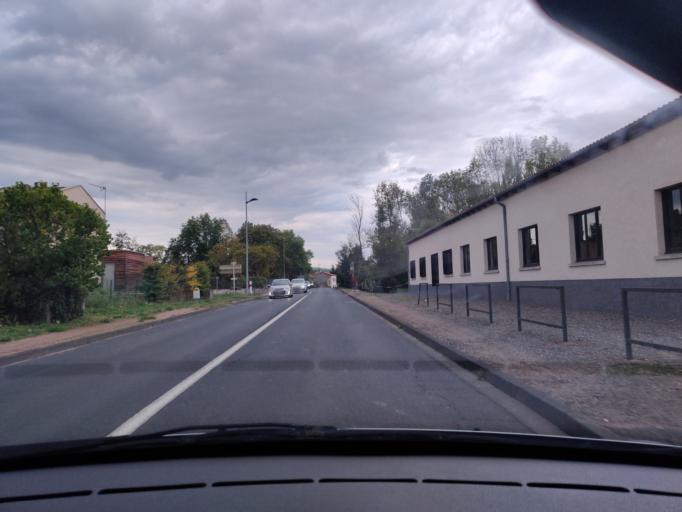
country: FR
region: Auvergne
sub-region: Departement du Puy-de-Dome
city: Saint-Bonnet-pres-Riom
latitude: 45.9445
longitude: 3.1104
